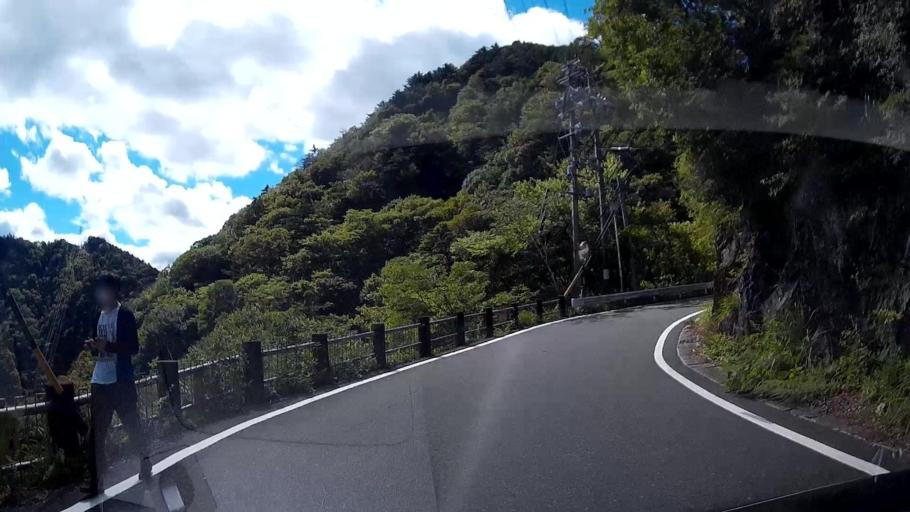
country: JP
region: Shizuoka
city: Shizuoka-shi
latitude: 35.2112
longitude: 138.2220
